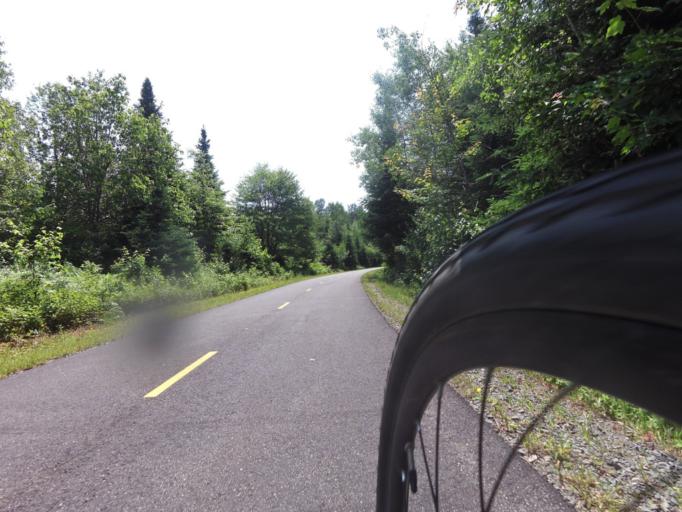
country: CA
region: Quebec
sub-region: Laurentides
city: Mont-Tremblant
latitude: 46.1584
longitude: -74.5995
